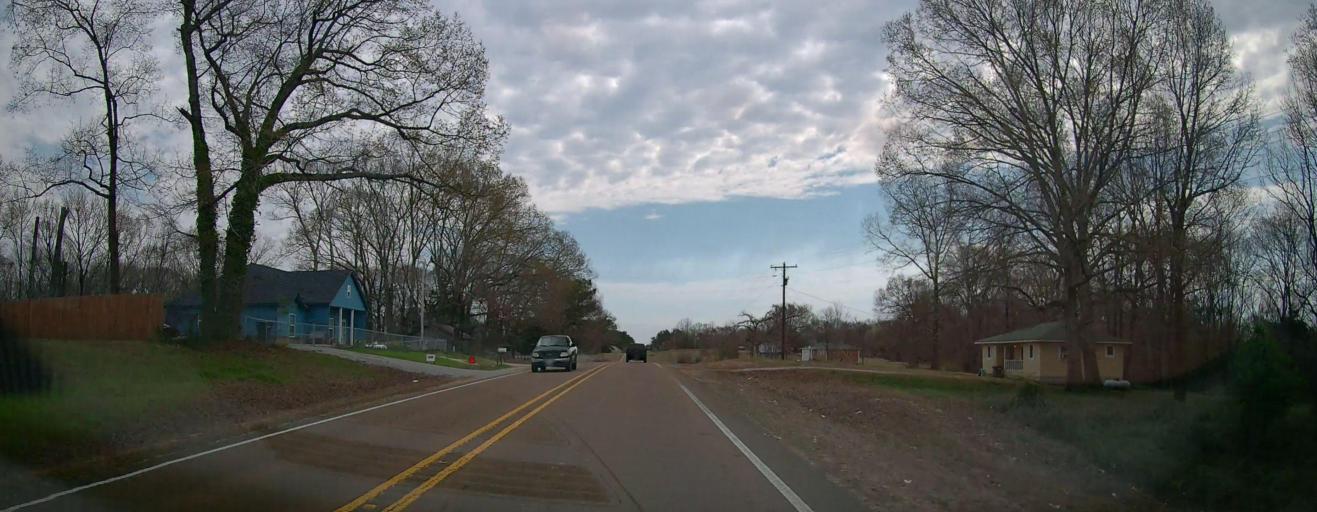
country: US
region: Mississippi
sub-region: Marshall County
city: Byhalia
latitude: 34.8435
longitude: -89.6098
